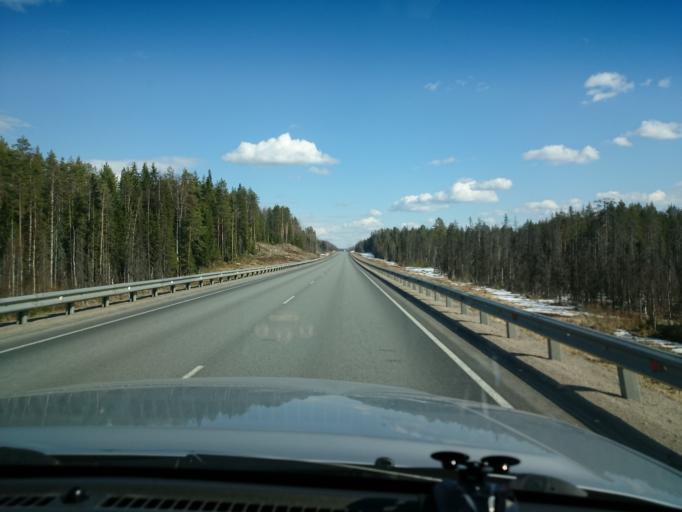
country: RU
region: Republic of Karelia
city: Pryazha
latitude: 61.5205
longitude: 33.4709
